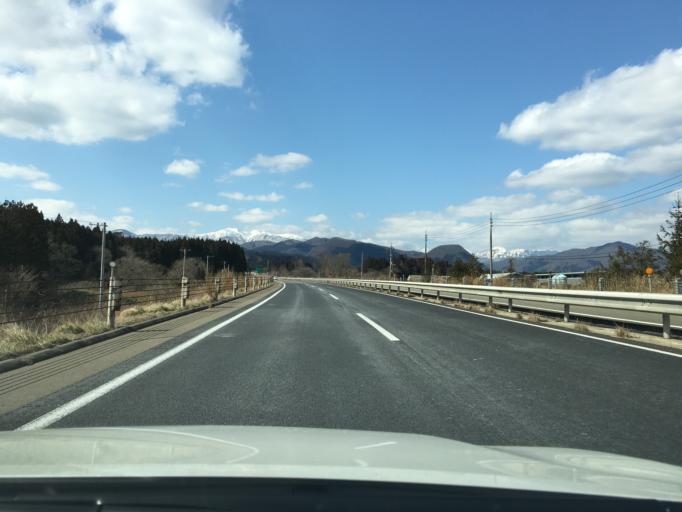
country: JP
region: Miyagi
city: Okawara
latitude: 38.1728
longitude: 140.6321
